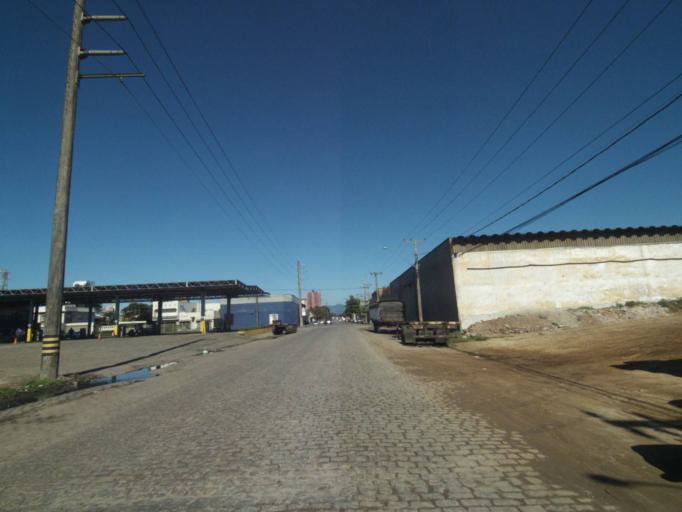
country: BR
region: Parana
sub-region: Paranagua
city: Paranagua
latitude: -25.5124
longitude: -48.5121
